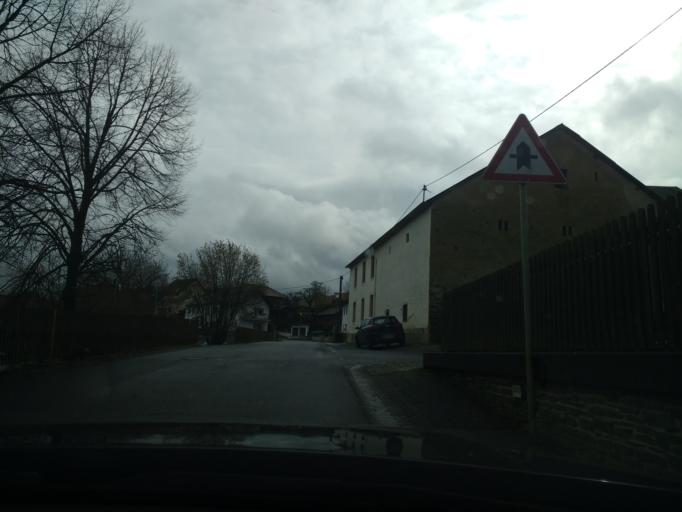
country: DE
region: Rheinland-Pfalz
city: Ollmuth
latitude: 49.6711
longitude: 6.7142
